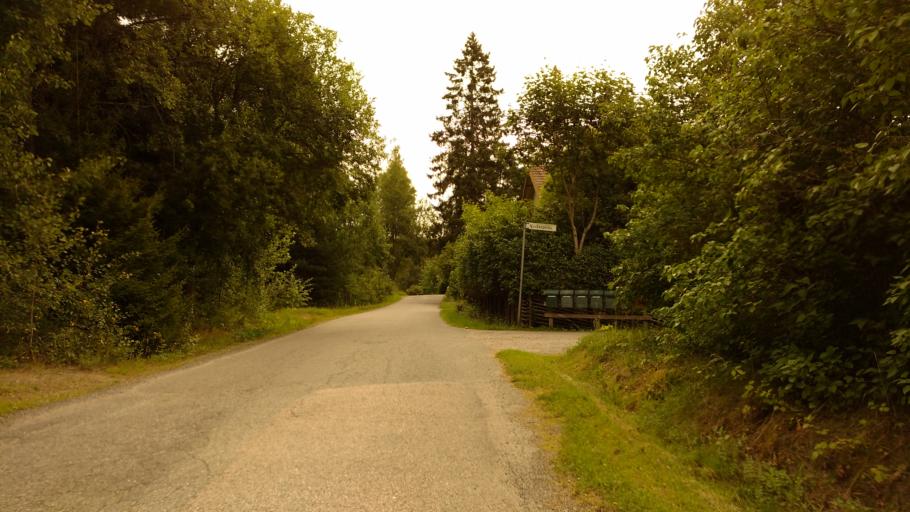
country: FI
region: Varsinais-Suomi
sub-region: Turku
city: Piikkioe
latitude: 60.4359
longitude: 22.4476
